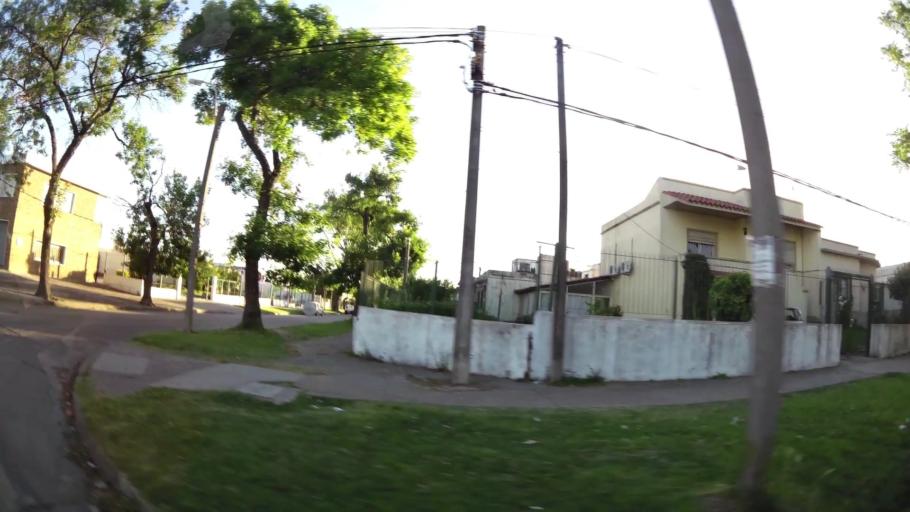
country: UY
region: Montevideo
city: Montevideo
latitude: -34.8394
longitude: -56.1904
